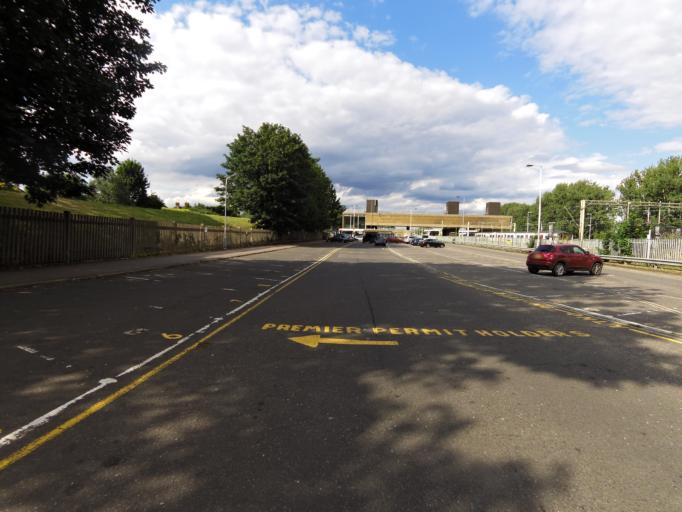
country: GB
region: England
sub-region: Hertfordshire
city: Broxbourne
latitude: 51.7459
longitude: -0.0118
